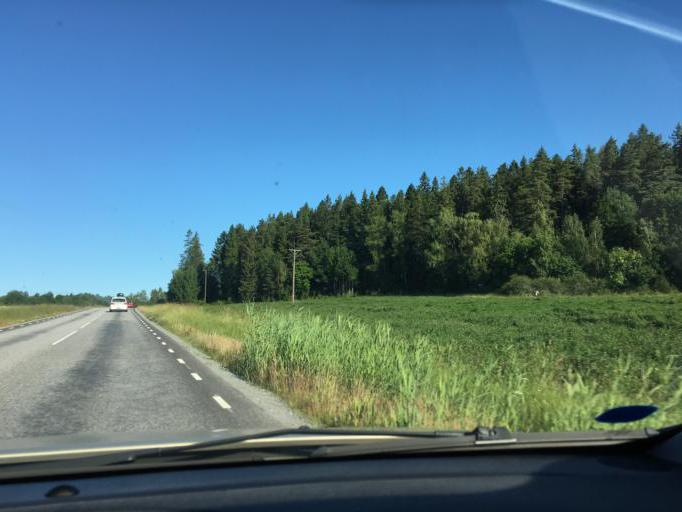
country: SE
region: Stockholm
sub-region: Salems Kommun
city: Ronninge
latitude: 59.2277
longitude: 17.7263
